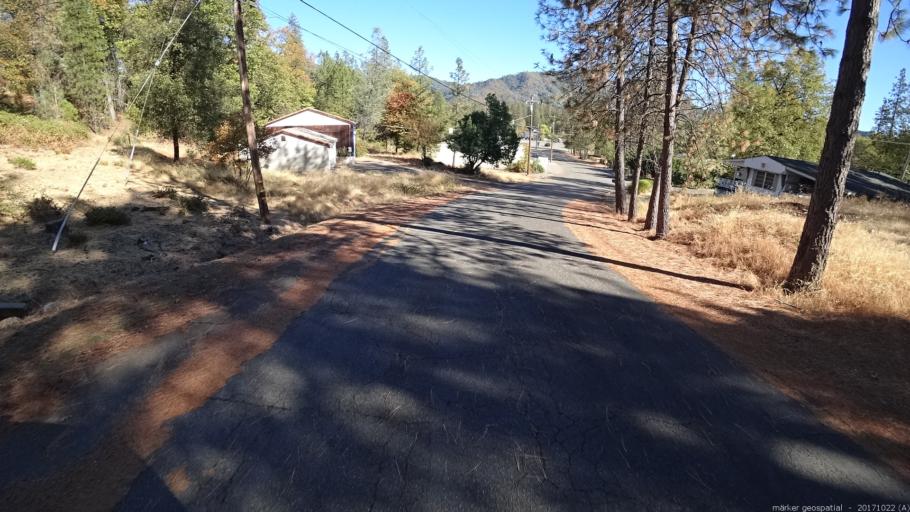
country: US
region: California
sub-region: Shasta County
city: Central Valley (historical)
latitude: 40.8899
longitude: -122.3862
